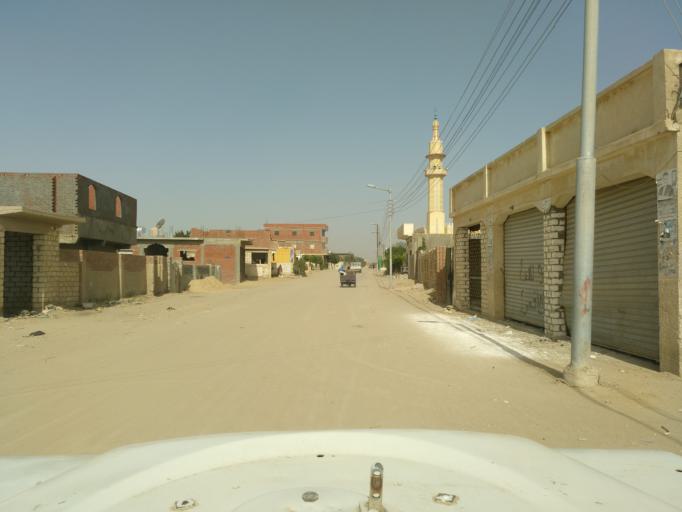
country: EG
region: Al Buhayrah
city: Beheira
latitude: 30.3826
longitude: 30.3428
